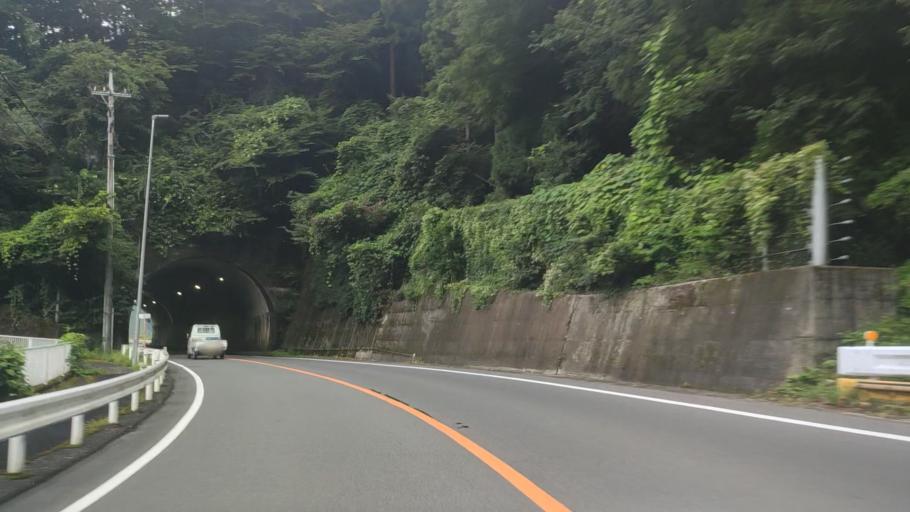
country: JP
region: Gunma
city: Omamacho-omama
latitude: 36.5465
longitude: 139.3710
